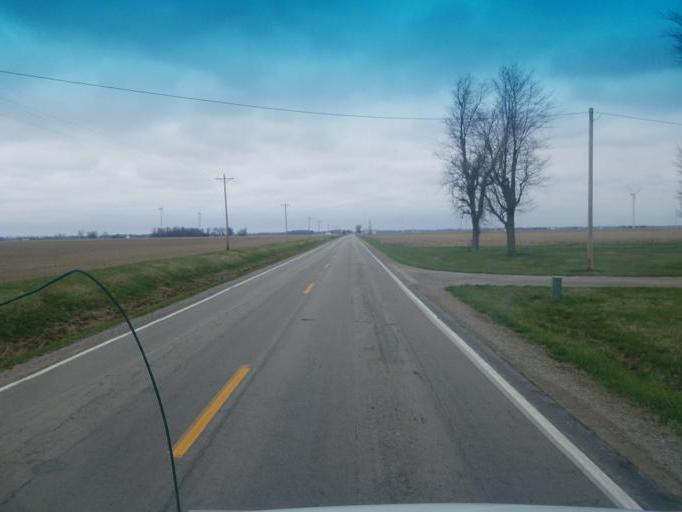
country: US
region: Ohio
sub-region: Paulding County
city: Payne
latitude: 41.0299
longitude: -84.7266
